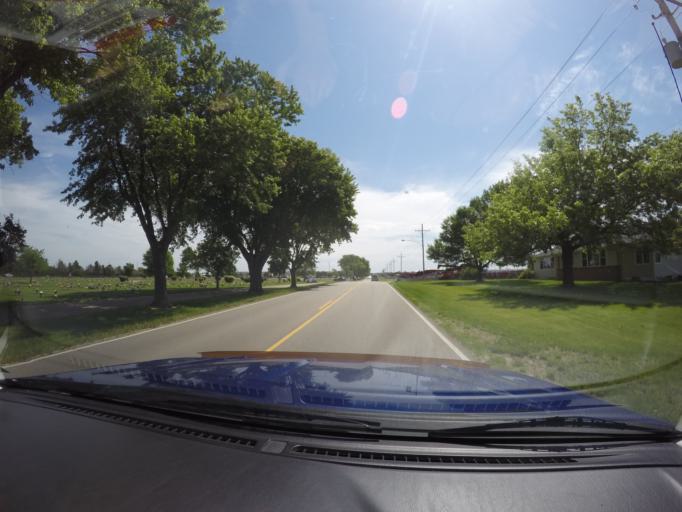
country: US
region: Nebraska
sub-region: Hall County
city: Grand Island
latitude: 40.9024
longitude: -98.3921
